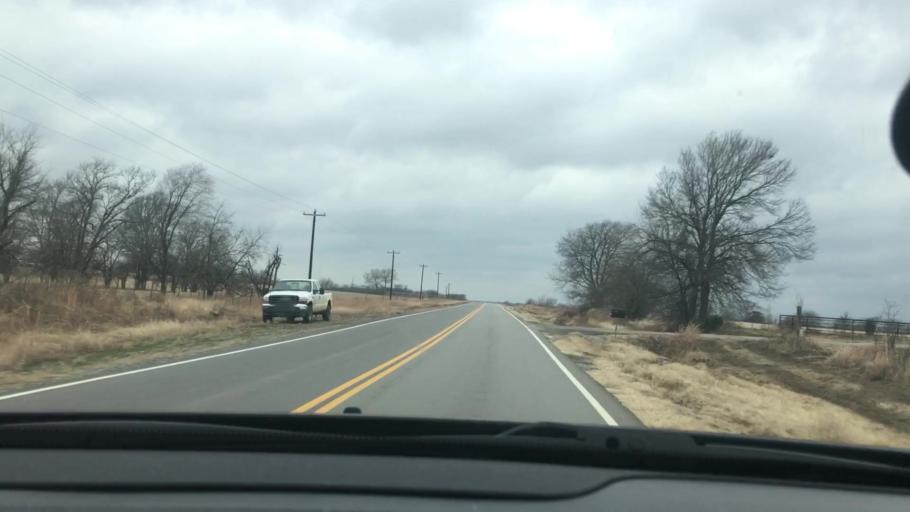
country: US
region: Oklahoma
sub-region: Atoka County
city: Atoka
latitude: 34.3788
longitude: -96.2891
